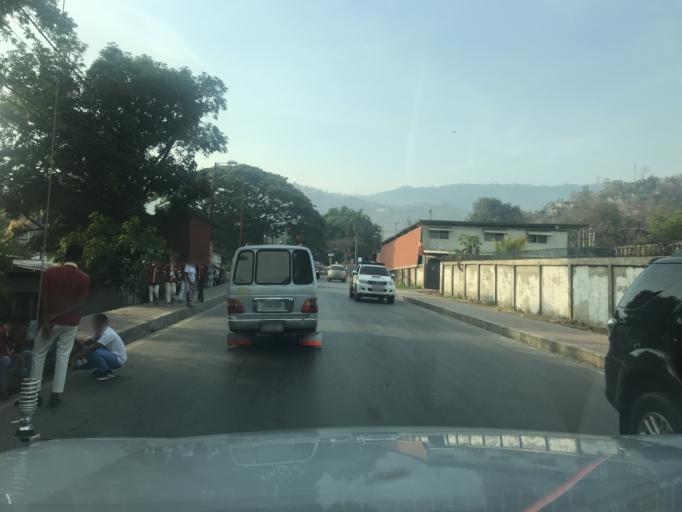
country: TL
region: Dili
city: Dili
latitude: -8.5646
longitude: 125.5816
